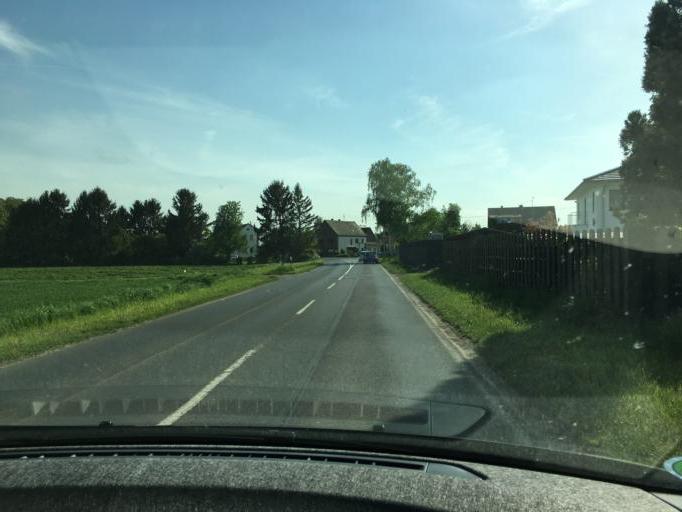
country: DE
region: North Rhine-Westphalia
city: Bornheim
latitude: 50.7852
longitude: 6.9551
